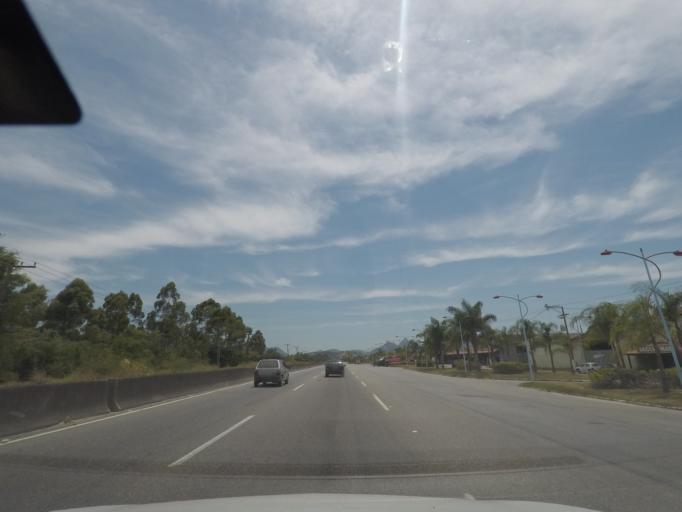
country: BR
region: Rio de Janeiro
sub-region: Marica
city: Marica
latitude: -22.9177
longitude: -42.8519
